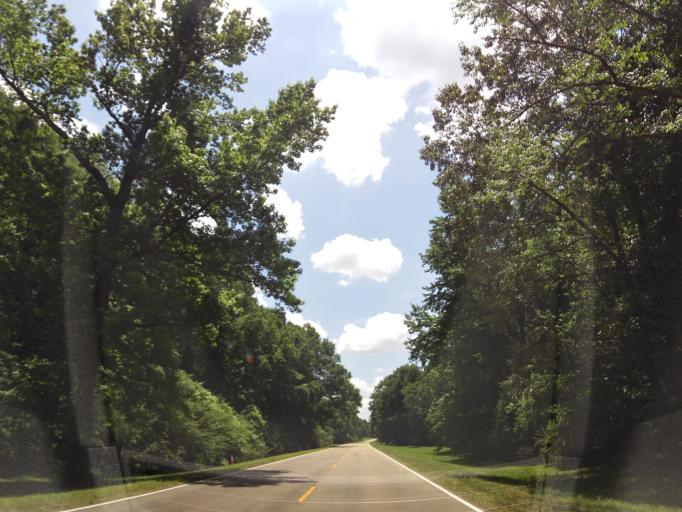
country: US
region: Mississippi
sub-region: Lee County
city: Tupelo
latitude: 34.2894
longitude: -88.7283
